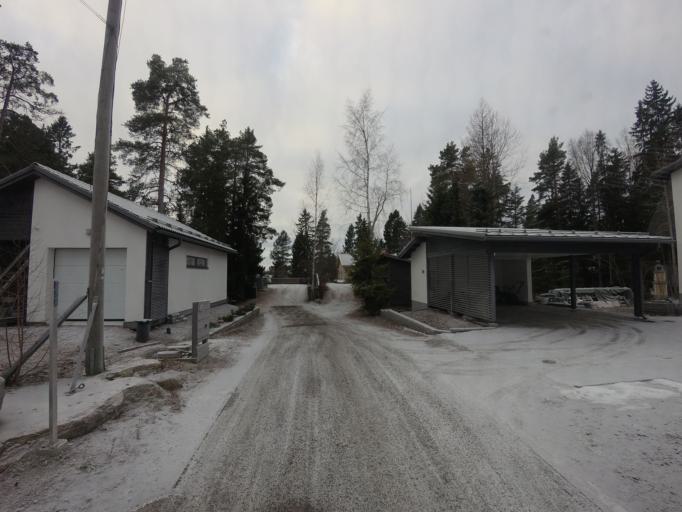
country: FI
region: Uusimaa
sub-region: Helsinki
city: Espoo
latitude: 60.2041
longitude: 24.6886
